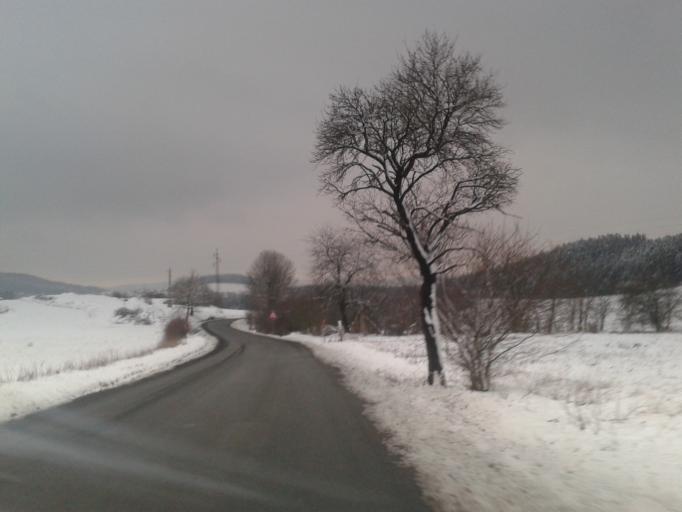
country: CZ
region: Central Bohemia
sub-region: Okres Beroun
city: Kraluv Dvur
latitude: 49.9299
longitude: 14.0610
